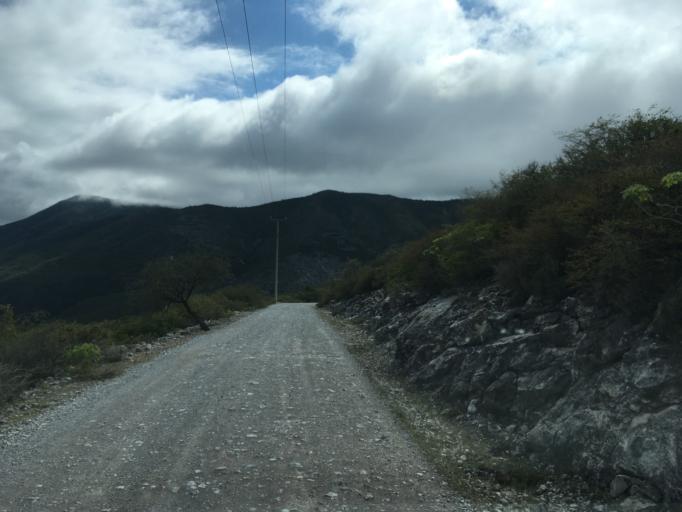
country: MX
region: Hidalgo
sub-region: Metztitlan
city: Fontezuelas
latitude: 20.6337
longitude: -98.8550
